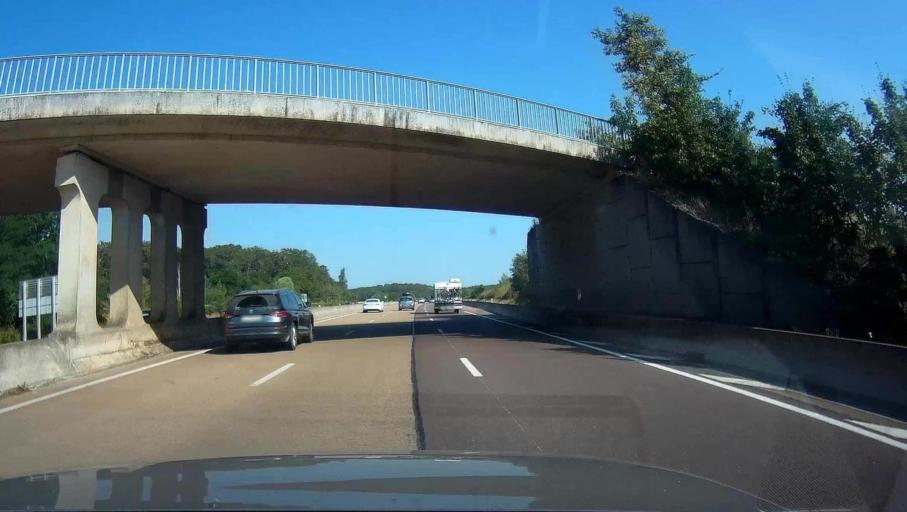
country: FR
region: Bourgogne
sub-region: Departement de la Cote-d'Or
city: Saint-Julien
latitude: 47.4301
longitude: 5.1685
